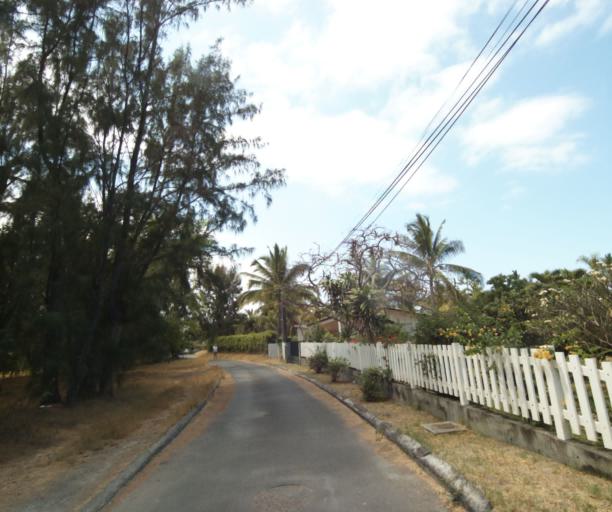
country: RE
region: Reunion
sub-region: Reunion
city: Trois-Bassins
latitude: -21.0894
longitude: 55.2326
